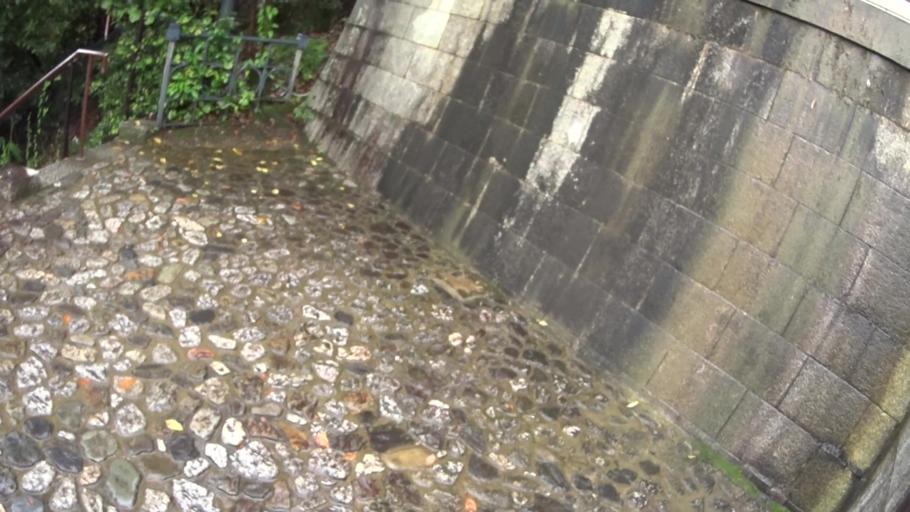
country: JP
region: Kyoto
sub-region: Kyoto-shi
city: Kamigyo-ku
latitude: 35.0137
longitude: 135.7953
